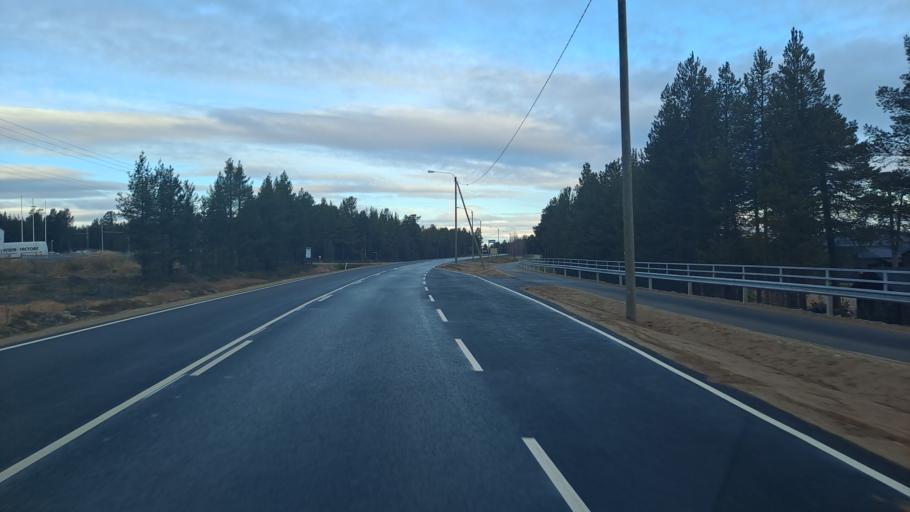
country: FI
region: Lapland
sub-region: Pohjois-Lappi
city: Inari
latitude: 68.8981
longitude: 27.0837
